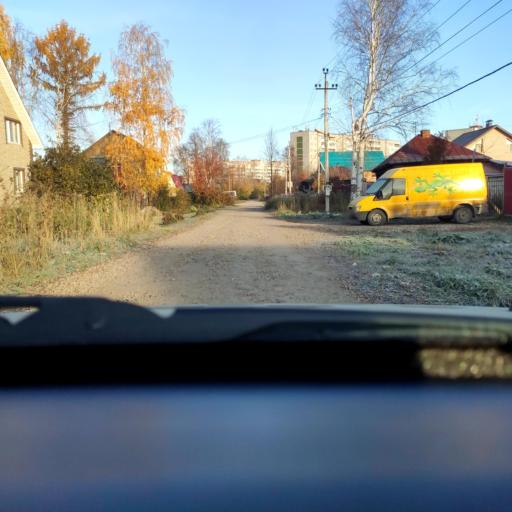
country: RU
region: Perm
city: Perm
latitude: 58.0261
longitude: 56.3266
